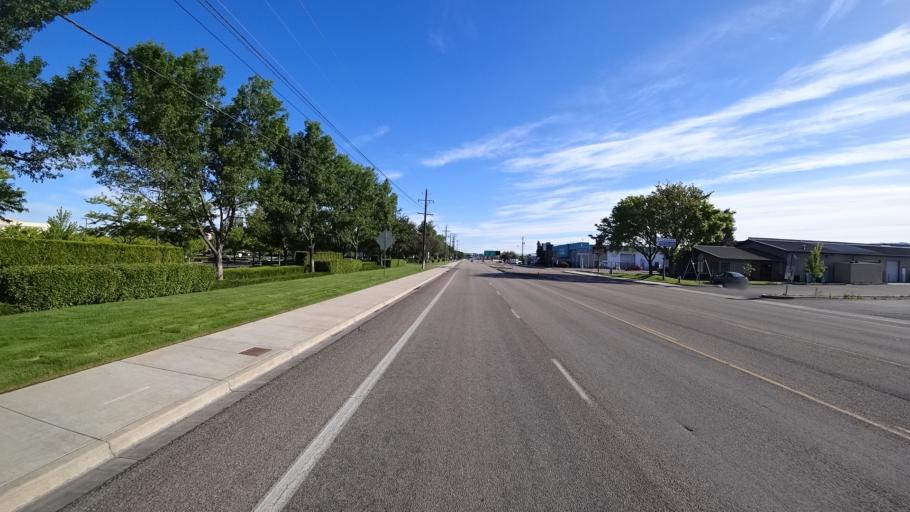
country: US
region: Idaho
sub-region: Ada County
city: Garden City
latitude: 43.5847
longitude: -116.2742
